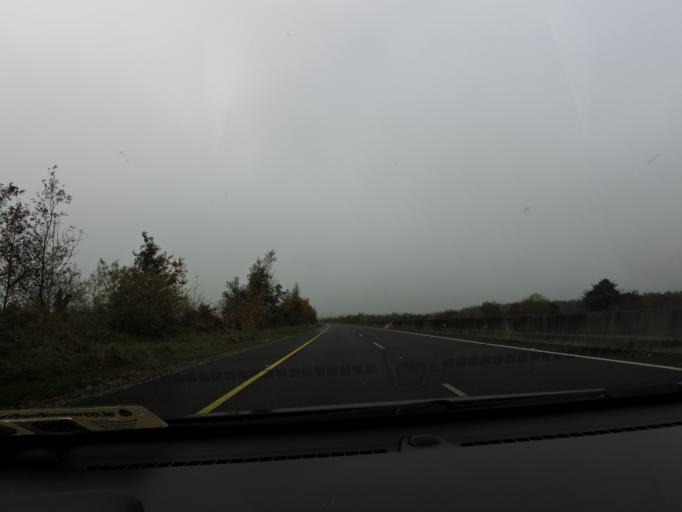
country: IE
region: Connaught
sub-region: County Galway
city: Ballinasloe
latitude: 53.3079
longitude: -8.3028
